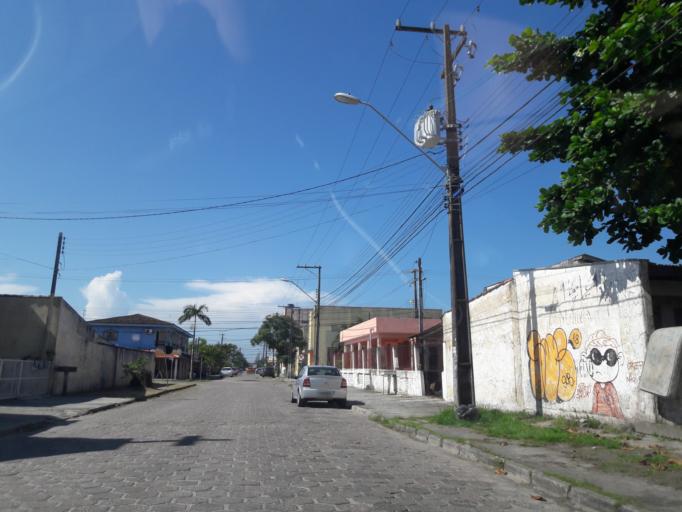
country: BR
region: Parana
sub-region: Pontal Do Parana
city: Pontal do Parana
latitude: -25.6995
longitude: -48.4728
